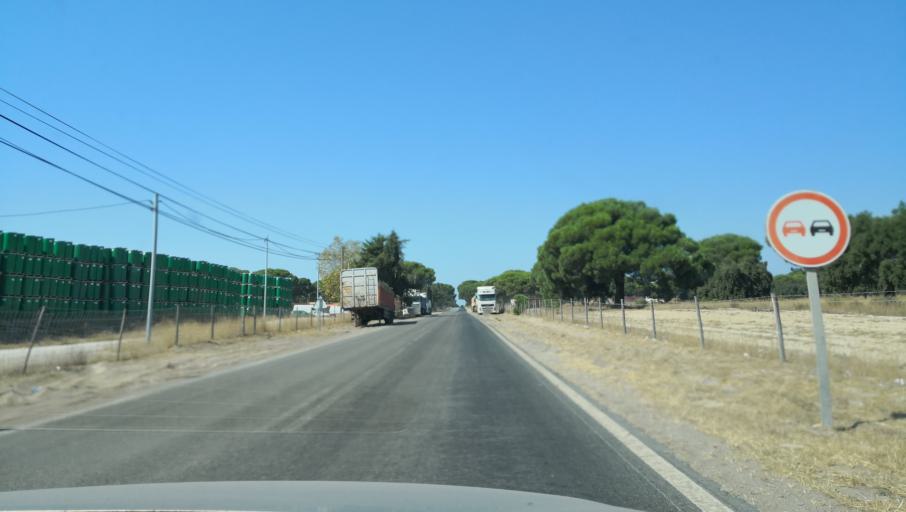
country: PT
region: Setubal
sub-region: Alcacer do Sal
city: Alcacer do Sal
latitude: 38.3715
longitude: -8.5498
